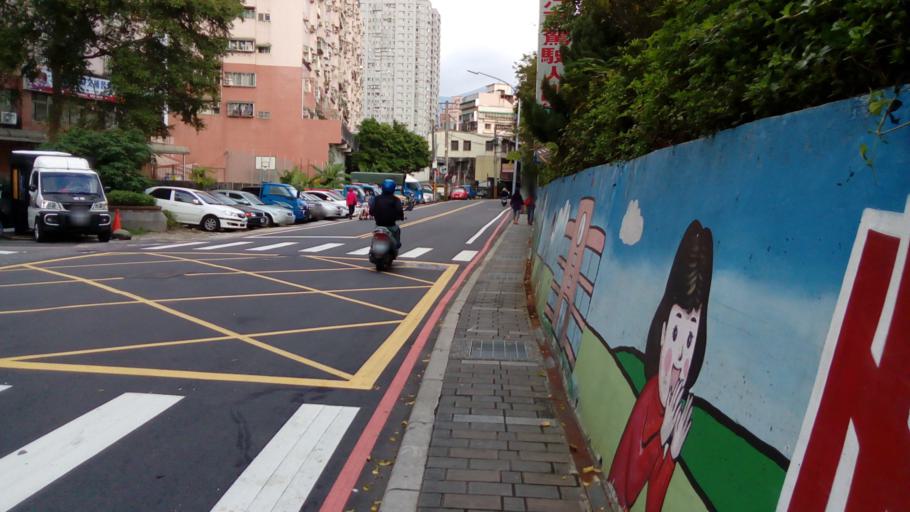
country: TW
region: Taipei
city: Taipei
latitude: 25.1796
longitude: 121.4406
